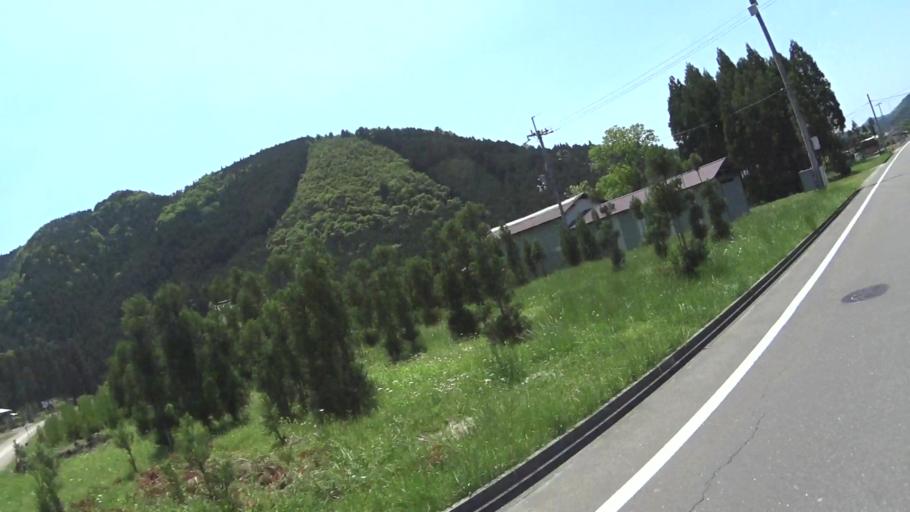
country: JP
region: Kyoto
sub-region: Kyoto-shi
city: Kamigyo-ku
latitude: 35.1748
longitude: 135.6535
